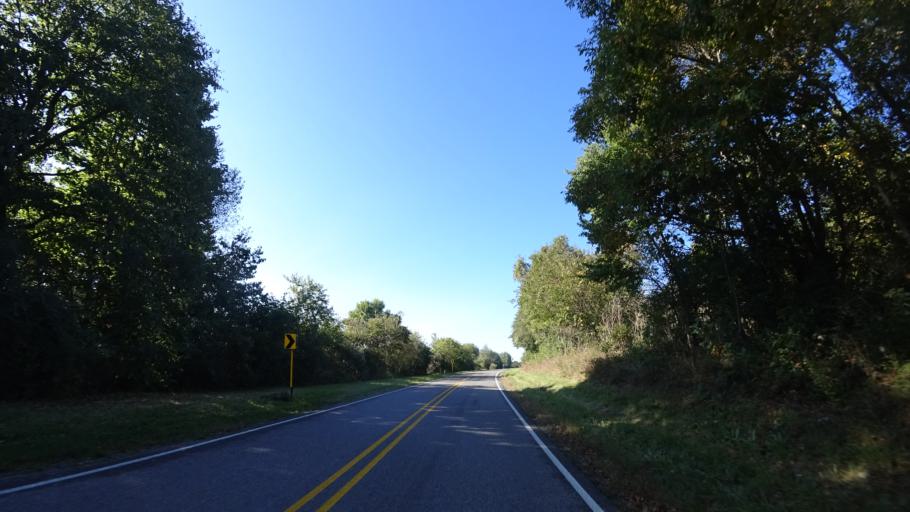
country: US
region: Michigan
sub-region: Berrien County
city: Benton Heights
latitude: 42.1525
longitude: -86.4228
